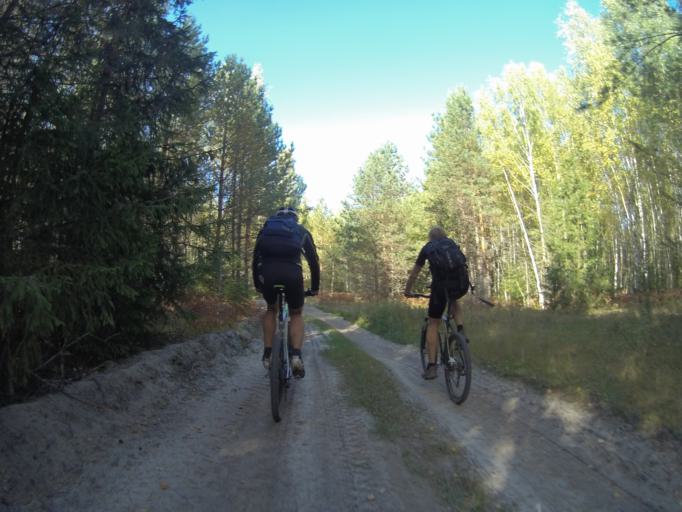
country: RU
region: Vladimir
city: Vorsha
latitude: 55.9106
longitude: 40.1599
